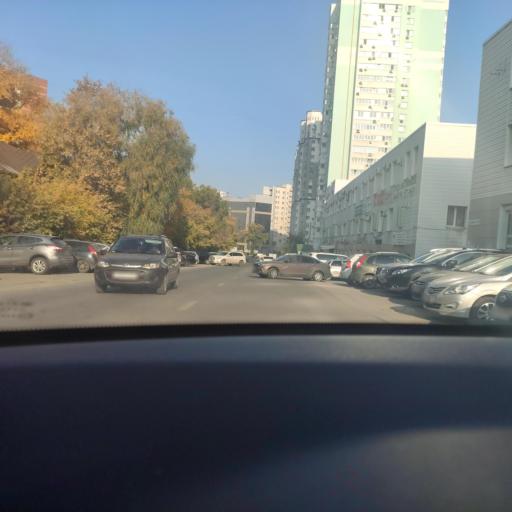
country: RU
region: Samara
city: Samara
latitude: 53.2197
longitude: 50.1948
